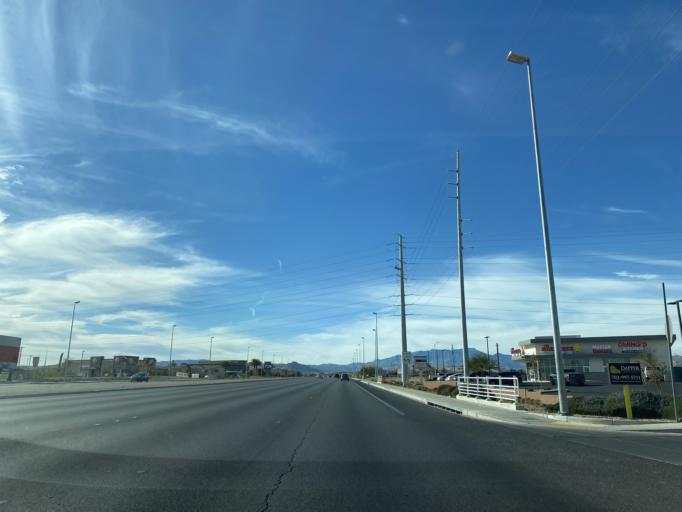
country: US
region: Nevada
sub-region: Clark County
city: Enterprise
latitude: 36.0315
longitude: -115.2107
